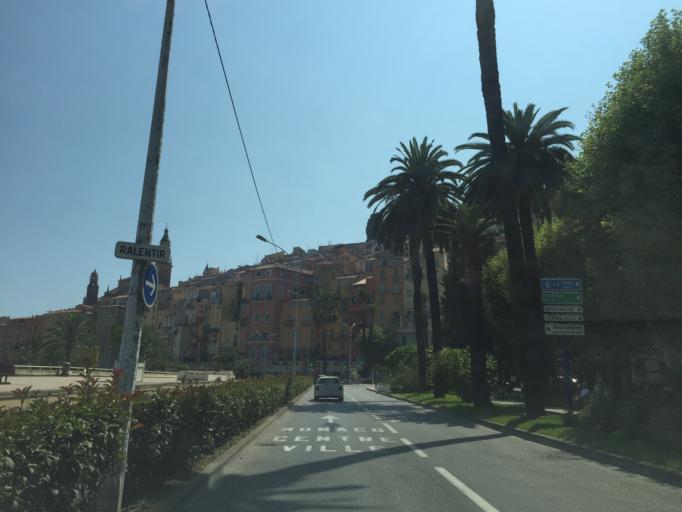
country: FR
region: Provence-Alpes-Cote d'Azur
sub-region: Departement des Alpes-Maritimes
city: Menton
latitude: 43.7797
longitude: 7.5081
